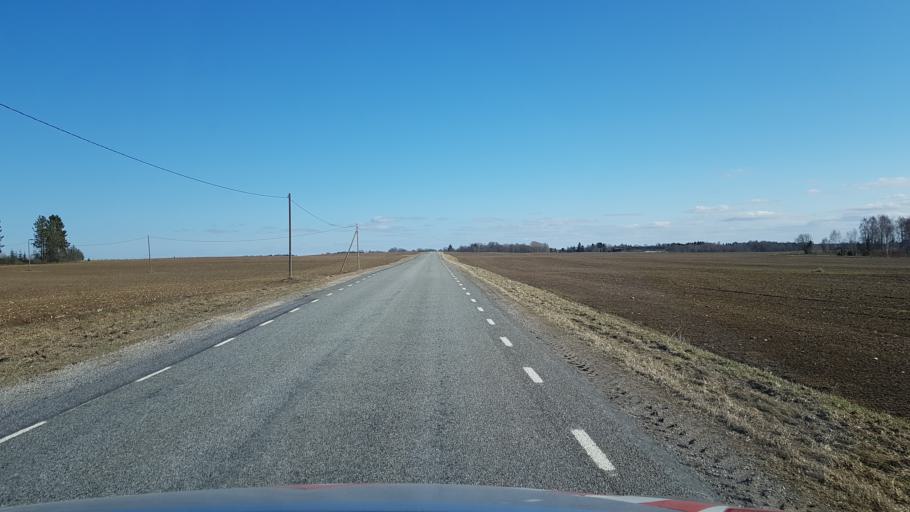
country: EE
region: Laeaene-Virumaa
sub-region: Kadrina vald
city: Kadrina
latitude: 59.3832
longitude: 26.0252
